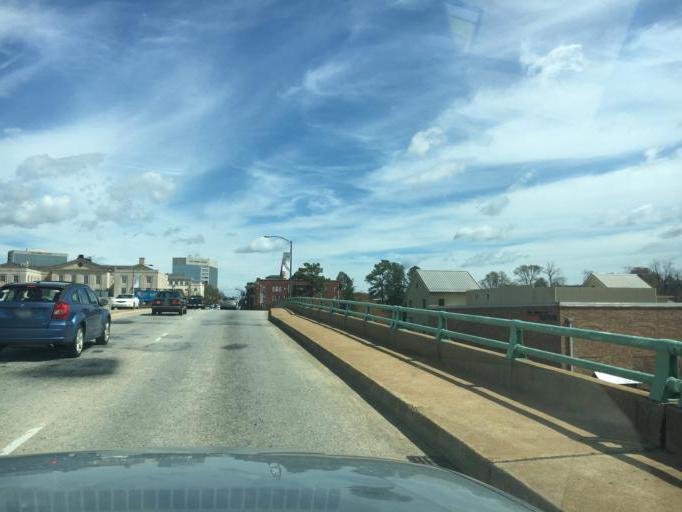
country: US
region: South Carolina
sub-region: Greenville County
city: Greenville
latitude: 34.8474
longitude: -82.3965
